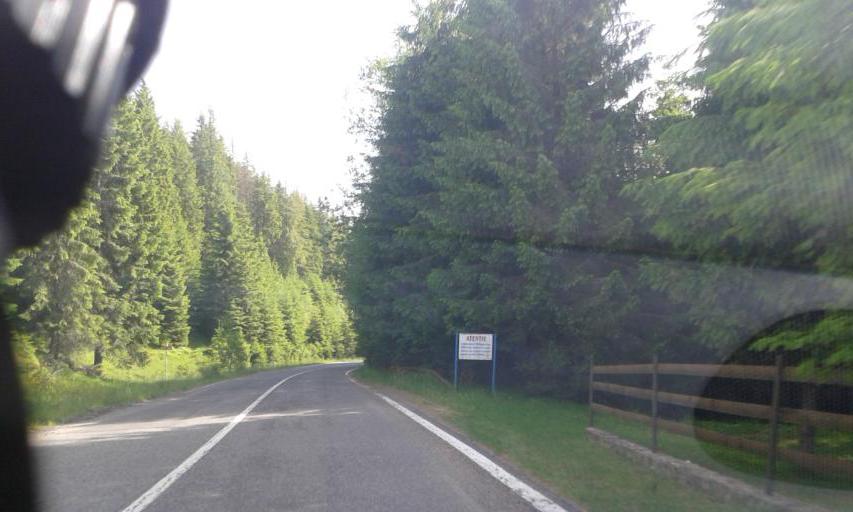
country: RO
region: Alba
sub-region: Comuna Sugag
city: Sugag
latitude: 45.5793
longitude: 23.6219
